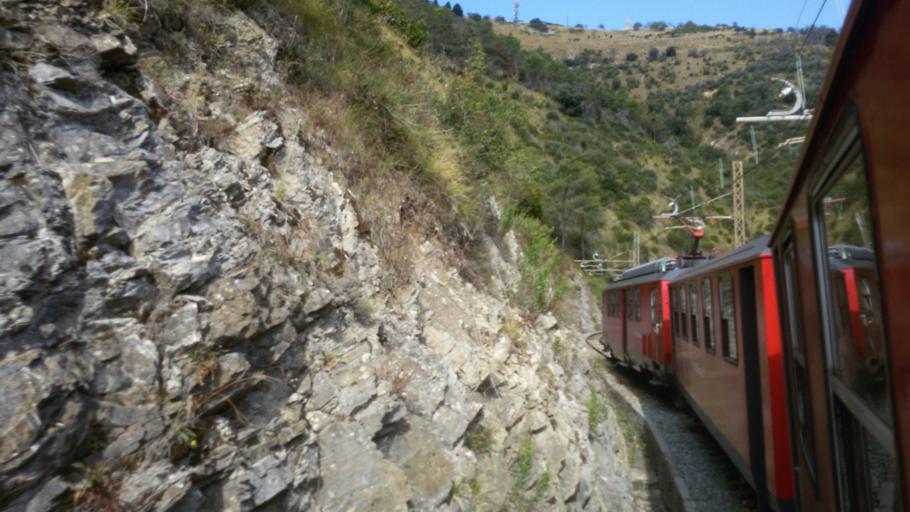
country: IT
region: Liguria
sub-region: Provincia di Genova
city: Genoa
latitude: 44.4382
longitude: 8.9377
